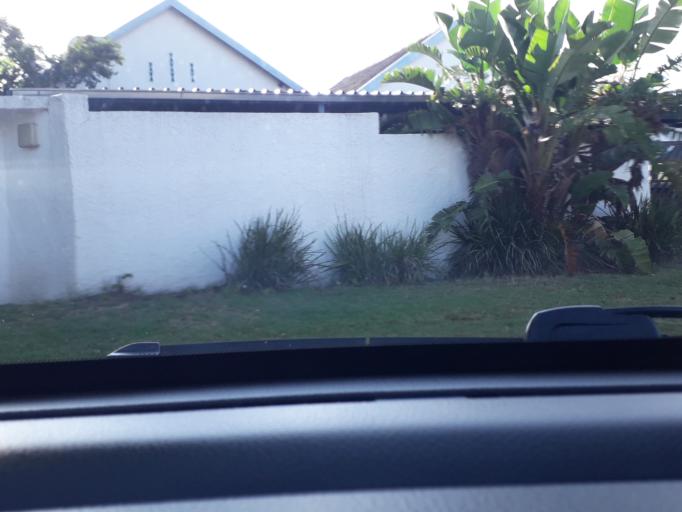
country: ZA
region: Gauteng
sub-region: City of Johannesburg Metropolitan Municipality
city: Modderfontein
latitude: -26.0775
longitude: 28.0850
